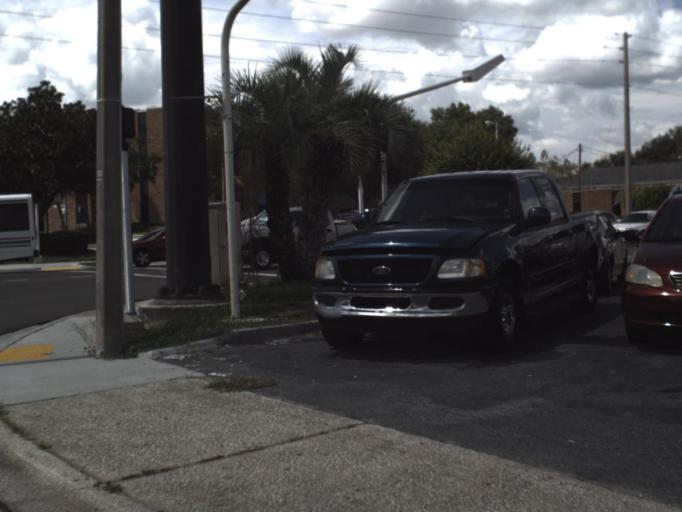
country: US
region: Florida
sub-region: Polk County
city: Winter Haven
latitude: 28.0041
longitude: -81.7182
